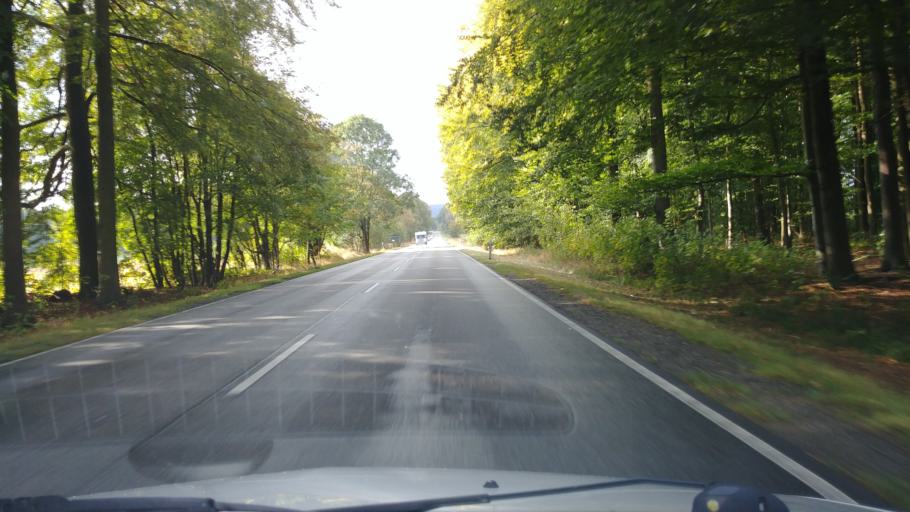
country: DE
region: Rheinland-Pfalz
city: Hochscheid
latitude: 49.9016
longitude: 7.2191
